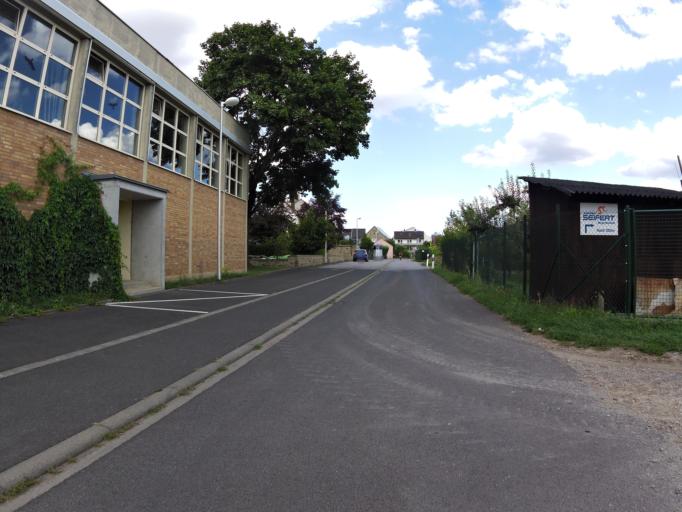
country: DE
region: Bavaria
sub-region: Regierungsbezirk Unterfranken
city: Bergrheinfeld
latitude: 50.0044
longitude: 10.1795
